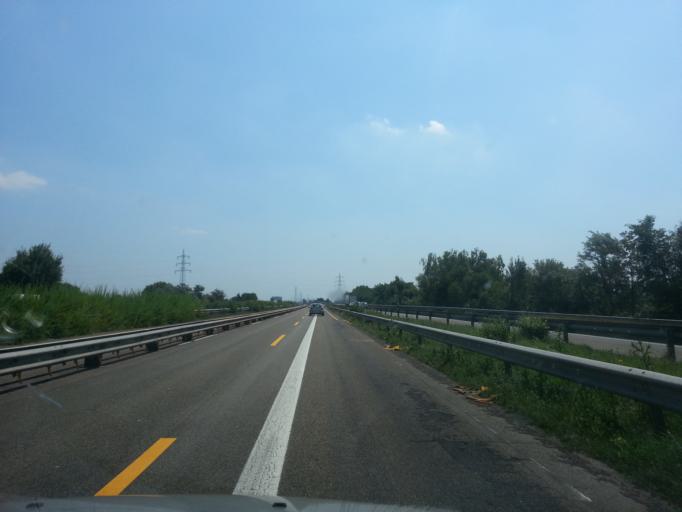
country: DE
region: Rheinland-Pfalz
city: Frankenthal
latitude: 49.5492
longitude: 8.3908
